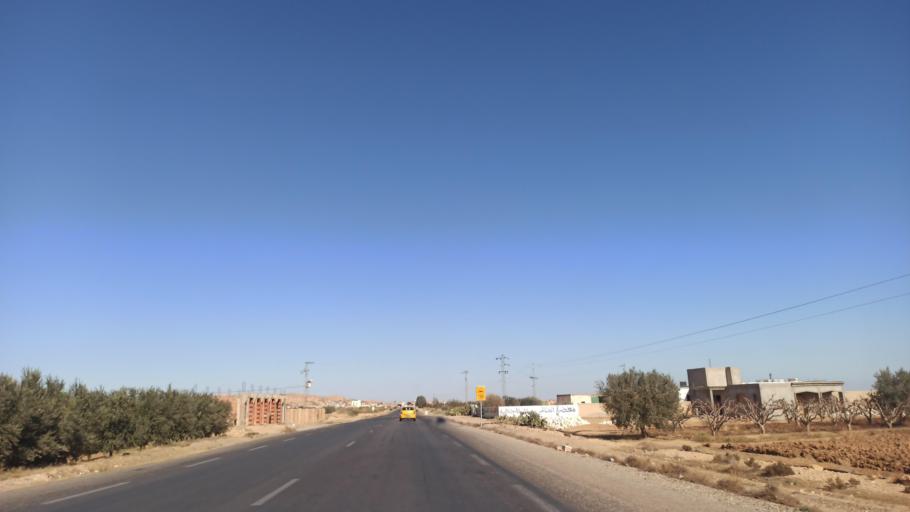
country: TN
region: Sidi Bu Zayd
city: Bi'r al Hufayy
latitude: 34.9030
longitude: 9.1765
